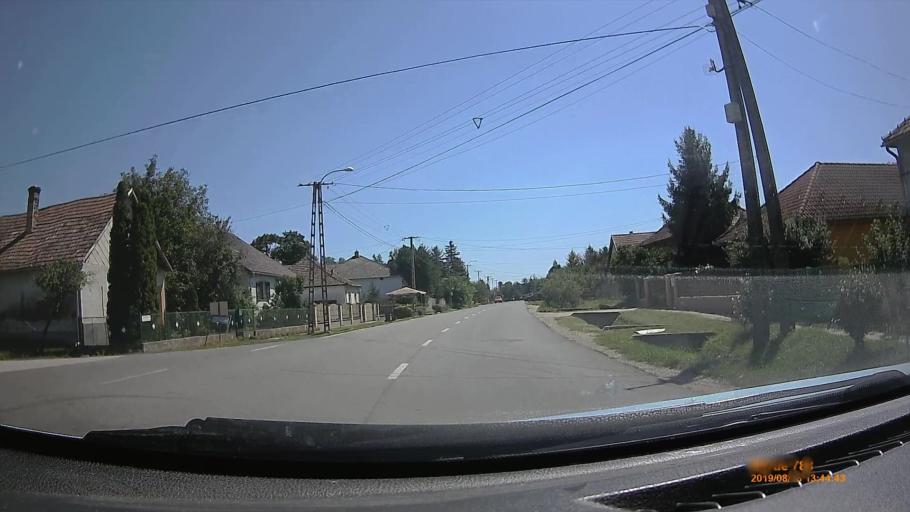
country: HU
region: Fejer
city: Cece
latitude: 46.7631
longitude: 18.6354
